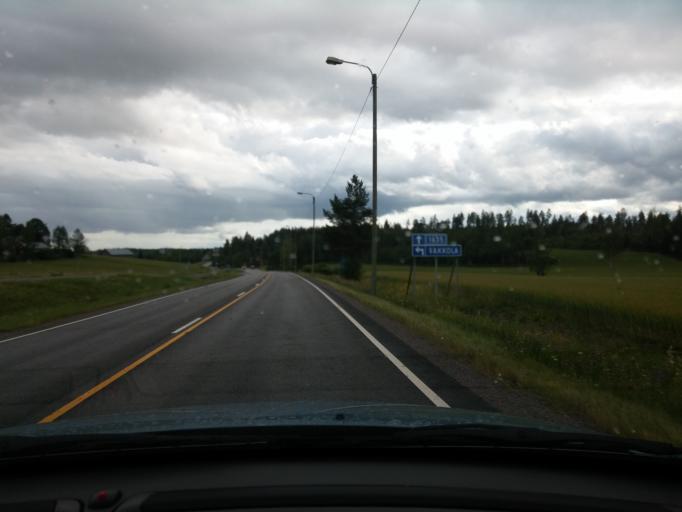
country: FI
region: Uusimaa
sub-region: Porvoo
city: Askola
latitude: 60.5223
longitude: 25.5797
